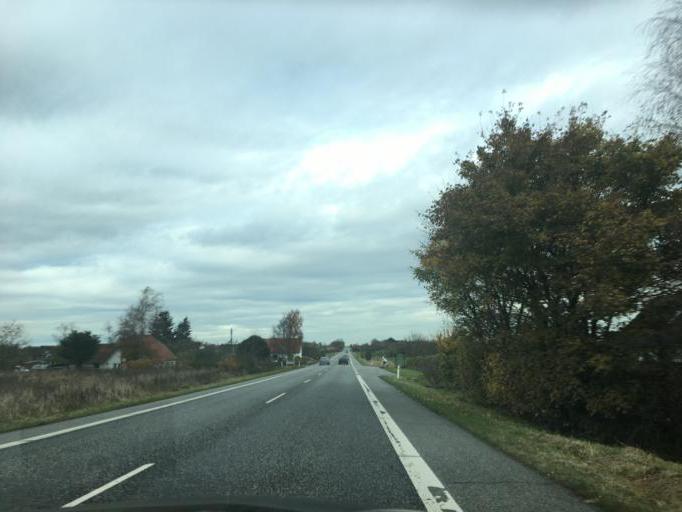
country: DK
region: South Denmark
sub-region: Vejle Kommune
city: Vejle
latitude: 55.6398
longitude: 9.4973
